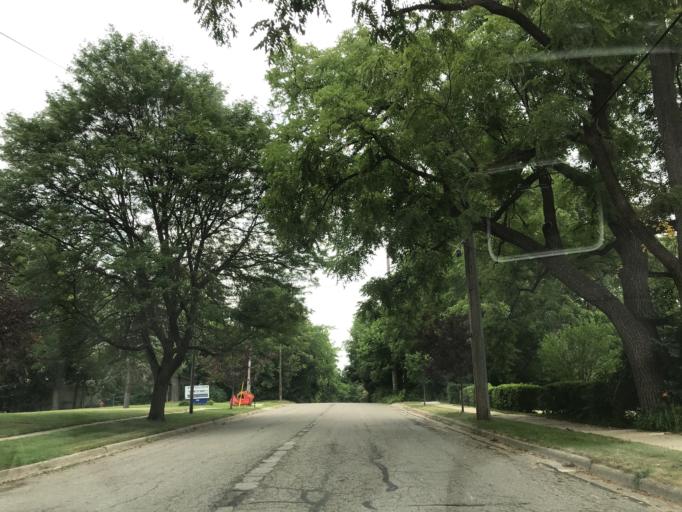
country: US
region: Michigan
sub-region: Washtenaw County
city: Ann Arbor
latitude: 42.2956
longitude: -83.7348
